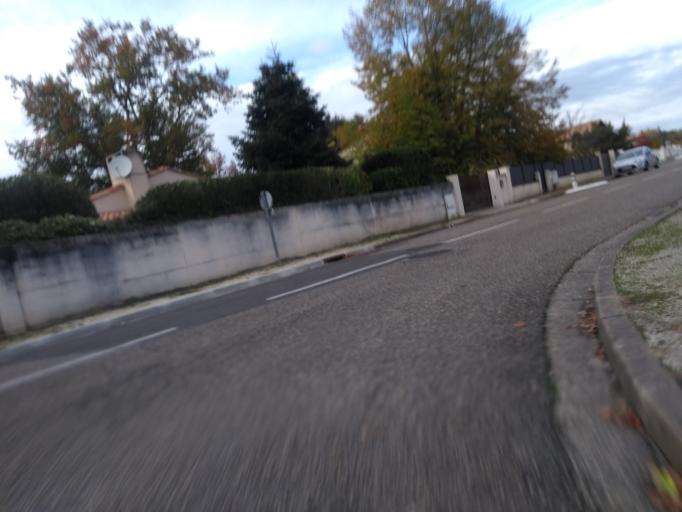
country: FR
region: Aquitaine
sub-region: Departement de la Gironde
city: Canejan
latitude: 44.7653
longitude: -0.6501
